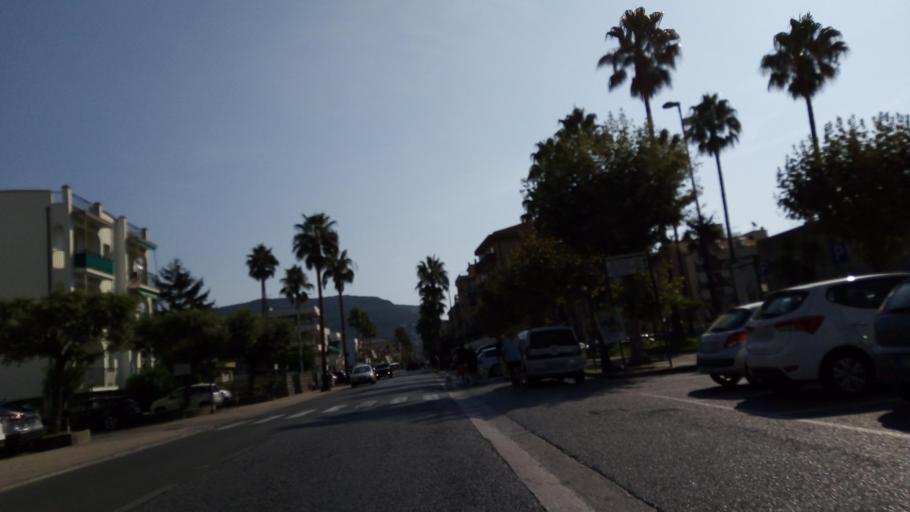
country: IT
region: Liguria
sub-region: Provincia di Savona
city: Pietra Ligure
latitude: 44.1547
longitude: 8.2927
